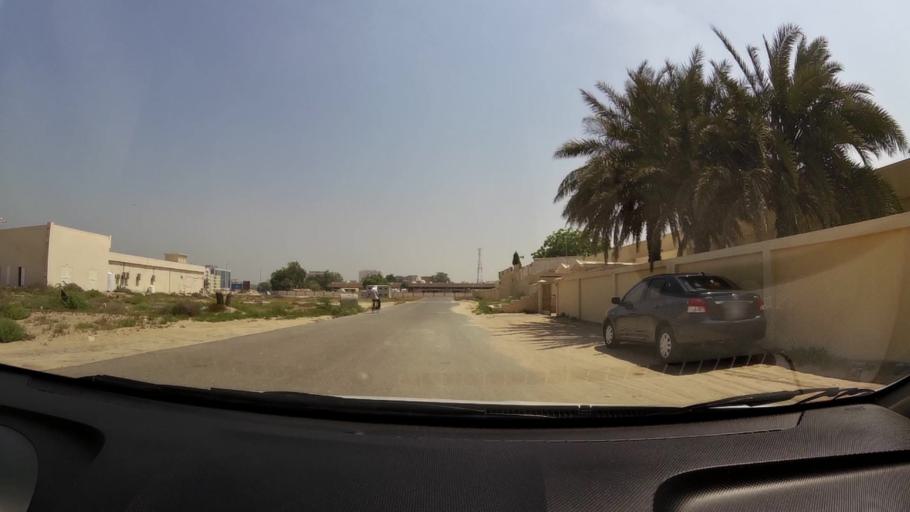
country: AE
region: Umm al Qaywayn
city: Umm al Qaywayn
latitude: 25.5718
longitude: 55.5582
